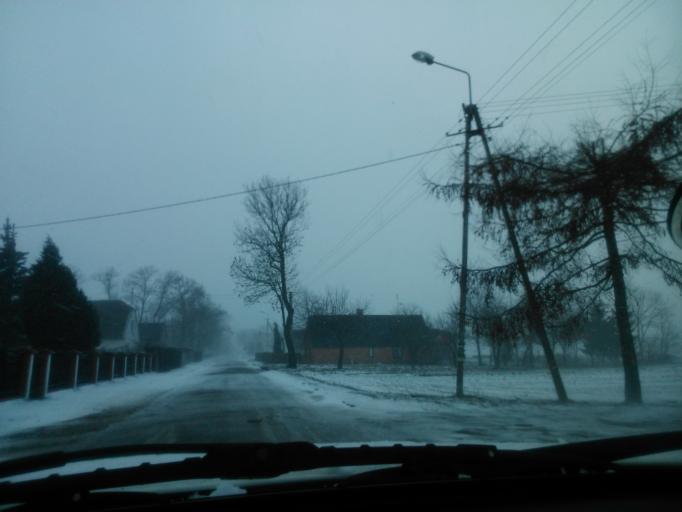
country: PL
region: Kujawsko-Pomorskie
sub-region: Powiat brodnicki
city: Bobrowo
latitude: 53.2798
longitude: 19.2364
